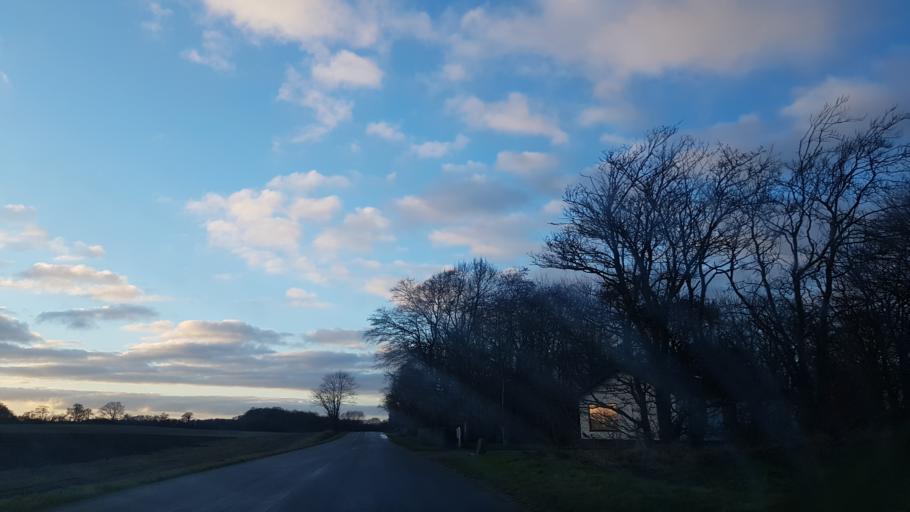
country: DK
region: South Denmark
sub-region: Kolding Kommune
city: Vamdrup
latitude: 55.3633
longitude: 9.3300
